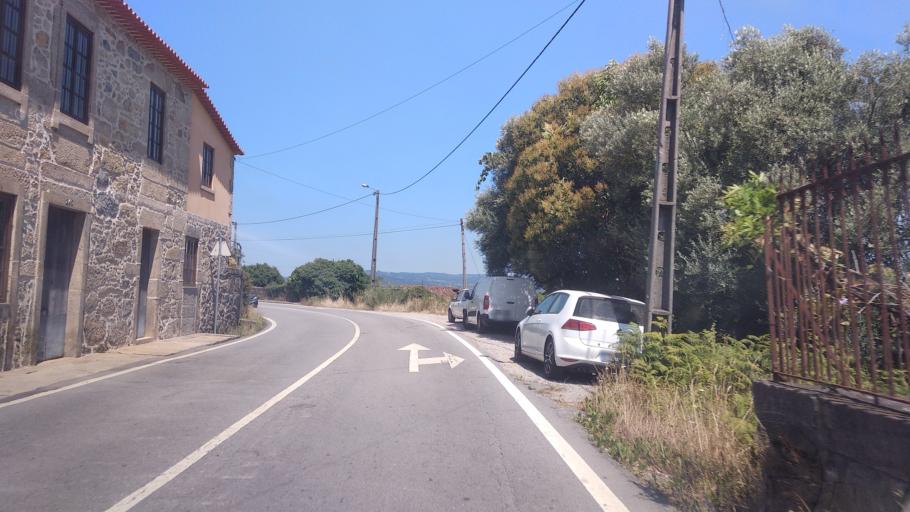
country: PT
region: Braga
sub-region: Braga
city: Adaufe
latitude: 41.5865
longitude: -8.3967
